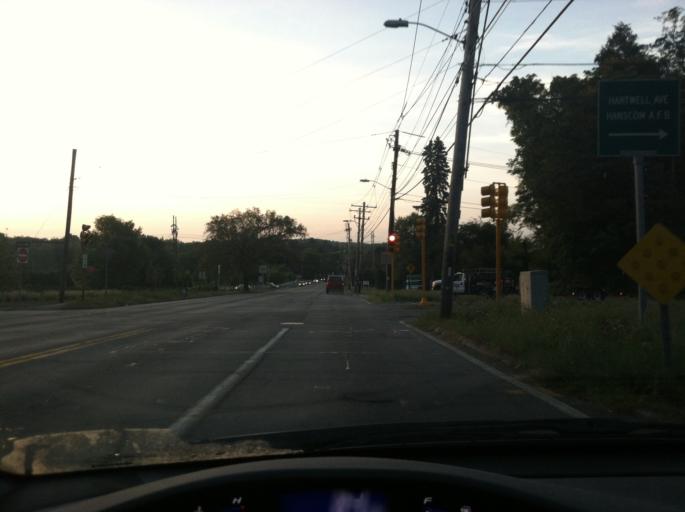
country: US
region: Massachusetts
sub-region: Middlesex County
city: Bedford
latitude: 42.4774
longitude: -71.2531
